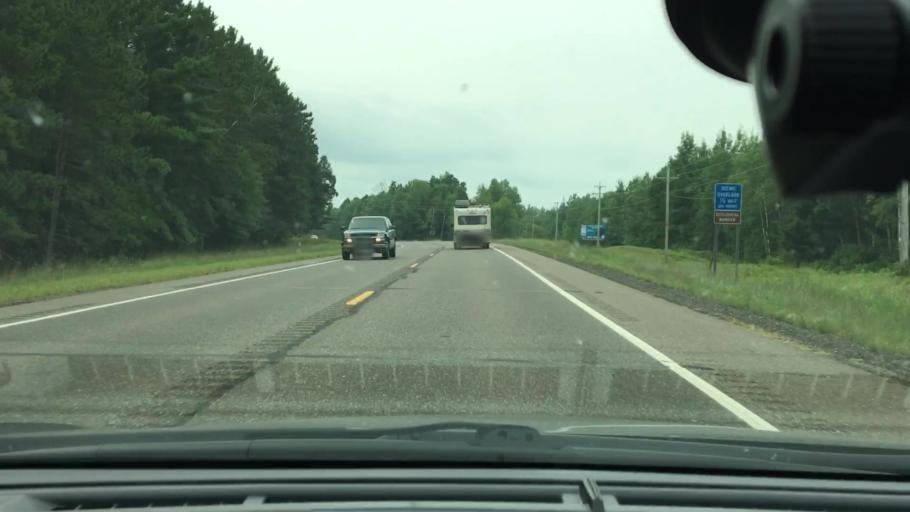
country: US
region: Minnesota
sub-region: Crow Wing County
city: Crosby
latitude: 46.4986
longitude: -93.9573
